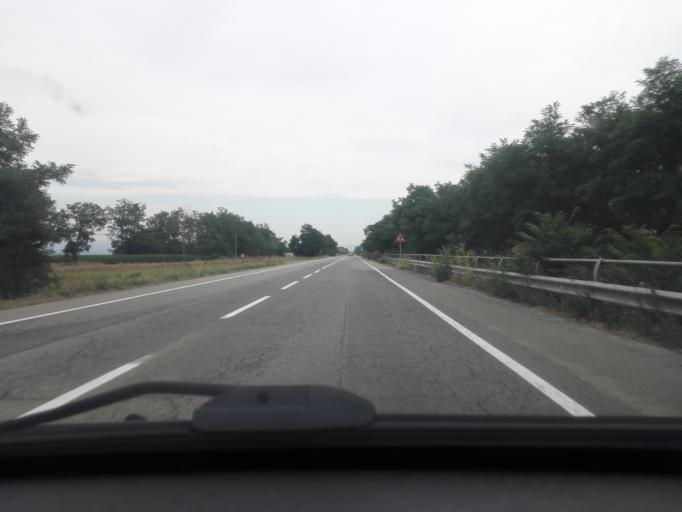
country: IT
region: Piedmont
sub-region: Provincia di Alessandria
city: Litta Parodi-Cascinagrossa
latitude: 44.8481
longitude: 8.7222
